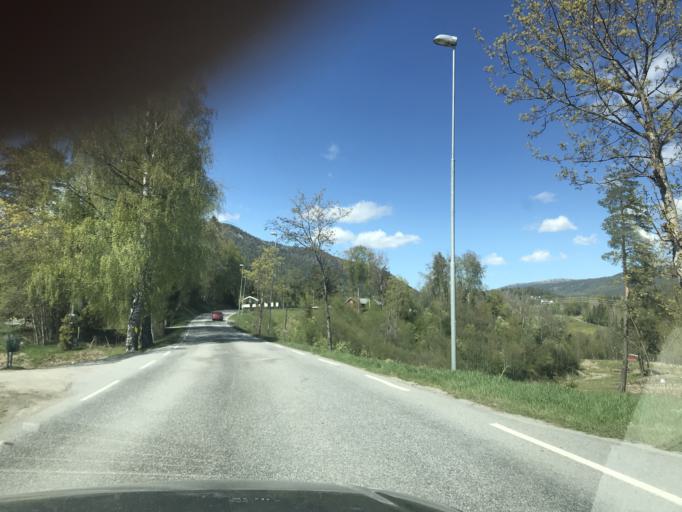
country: NO
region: Telemark
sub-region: Hjartdal
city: Sauland
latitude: 59.6175
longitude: 8.9480
